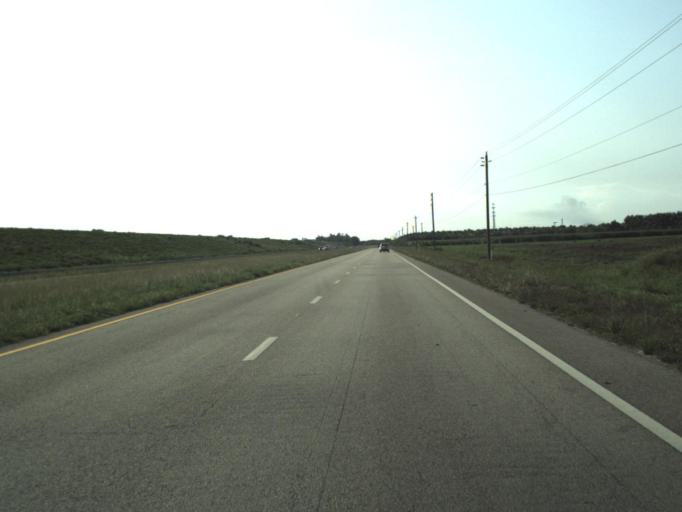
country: US
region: Florida
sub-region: Hendry County
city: Clewiston
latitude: 26.7091
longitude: -80.8334
